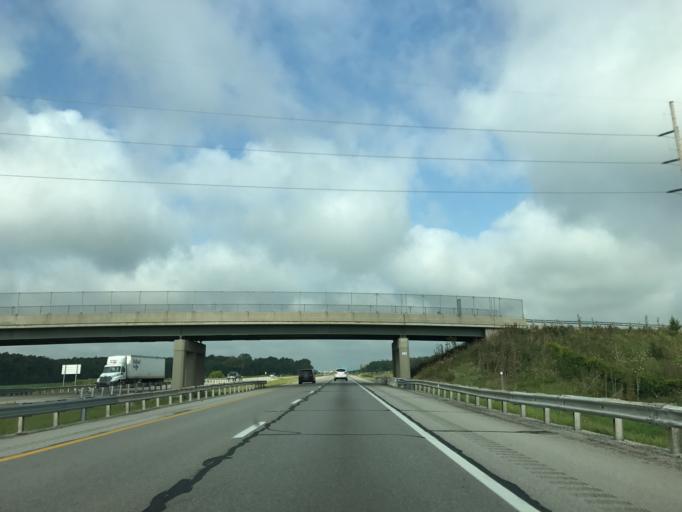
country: US
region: Ohio
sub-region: Williams County
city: Pioneer
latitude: 41.6097
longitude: -84.5158
